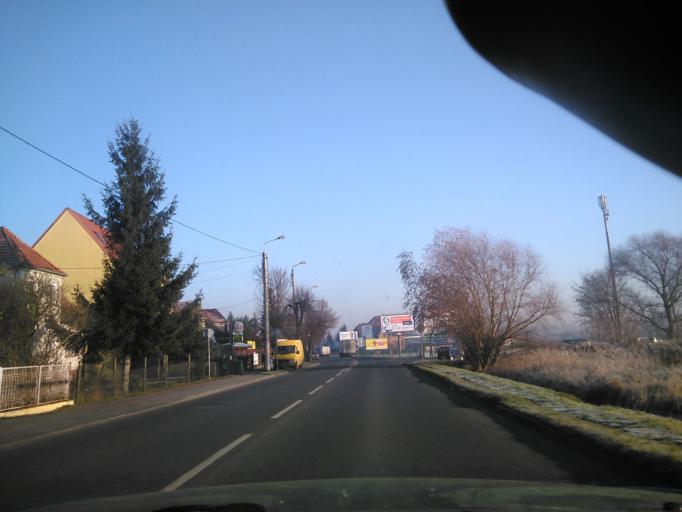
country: PL
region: Lower Silesian Voivodeship
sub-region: Powiat wroclawski
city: Bielany Wroclawskie
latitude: 51.0574
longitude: 16.9722
